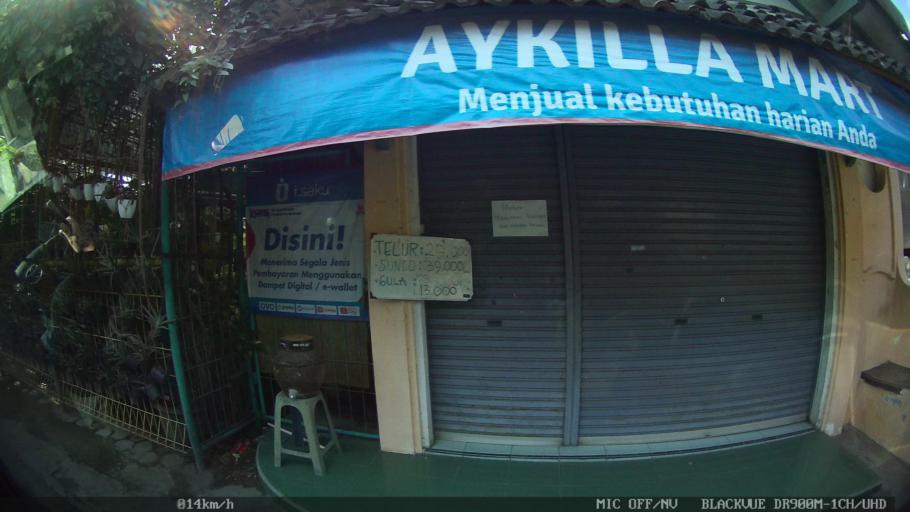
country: ID
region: Daerah Istimewa Yogyakarta
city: Sewon
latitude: -7.8339
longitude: 110.4037
